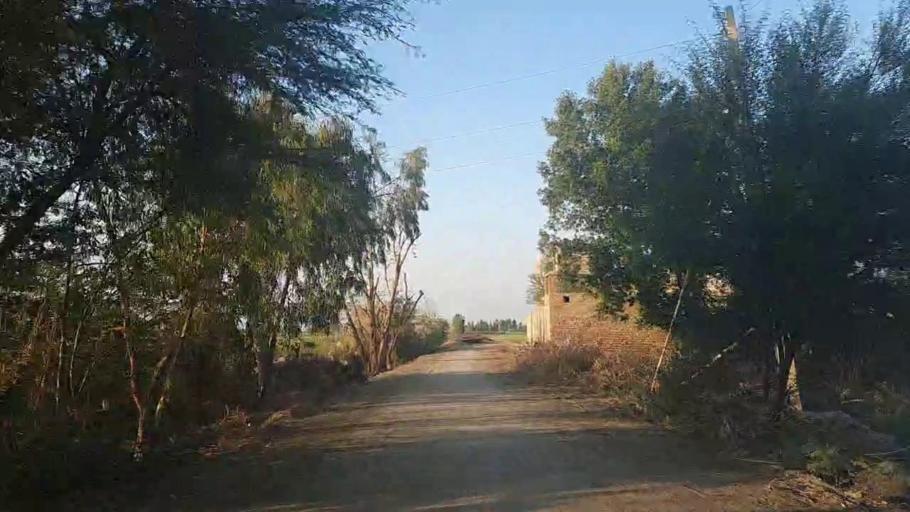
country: PK
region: Sindh
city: Jam Sahib
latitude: 26.3433
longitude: 68.6917
